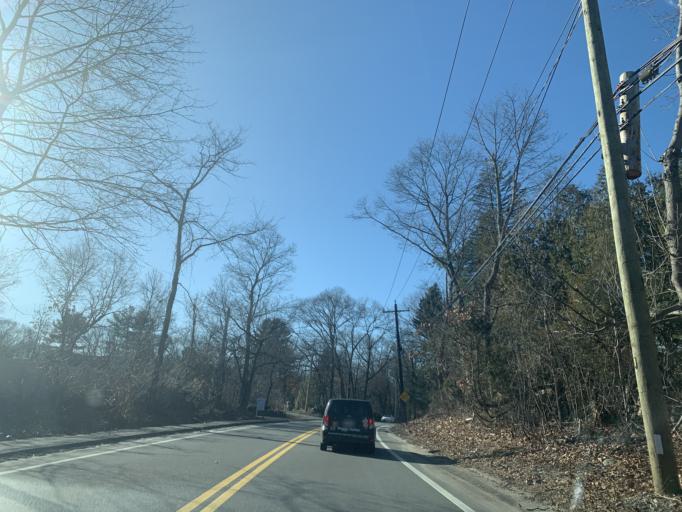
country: US
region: Massachusetts
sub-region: Middlesex County
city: Wayland
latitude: 42.3605
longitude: -71.3357
